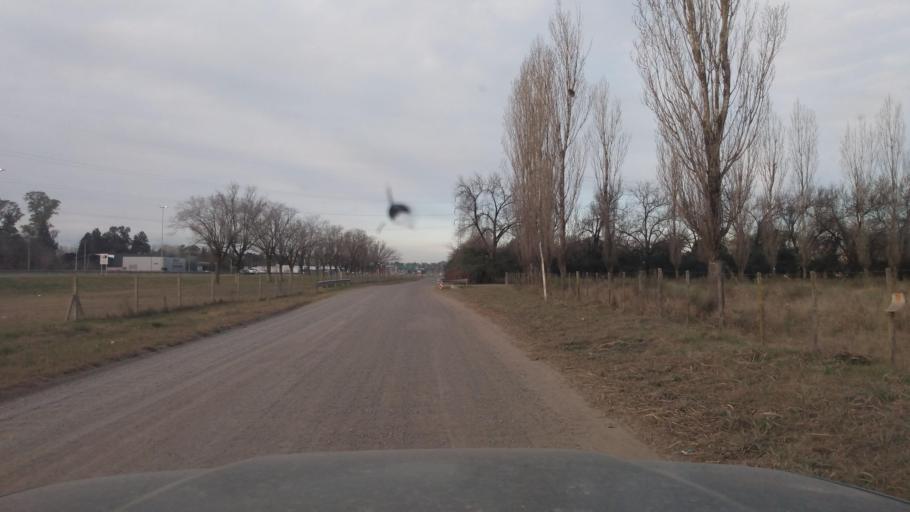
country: AR
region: Buenos Aires
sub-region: Partido de Lujan
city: Lujan
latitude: -34.5738
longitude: -59.0743
